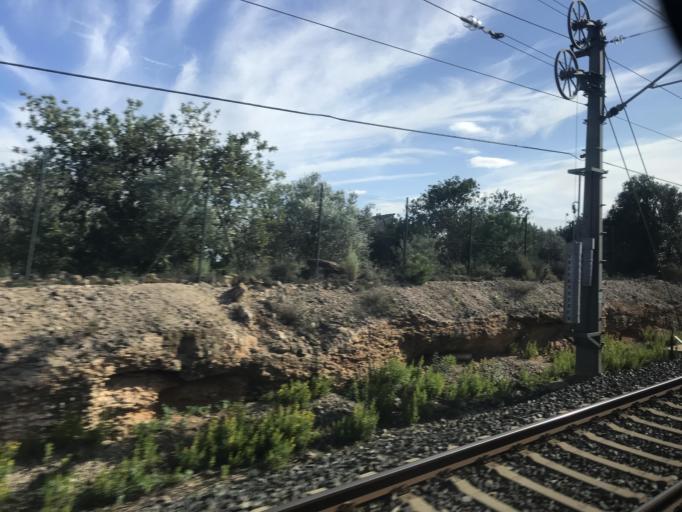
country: ES
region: Catalonia
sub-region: Provincia de Tarragona
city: l'Ametlla de Mar
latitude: 40.8810
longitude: 0.7956
